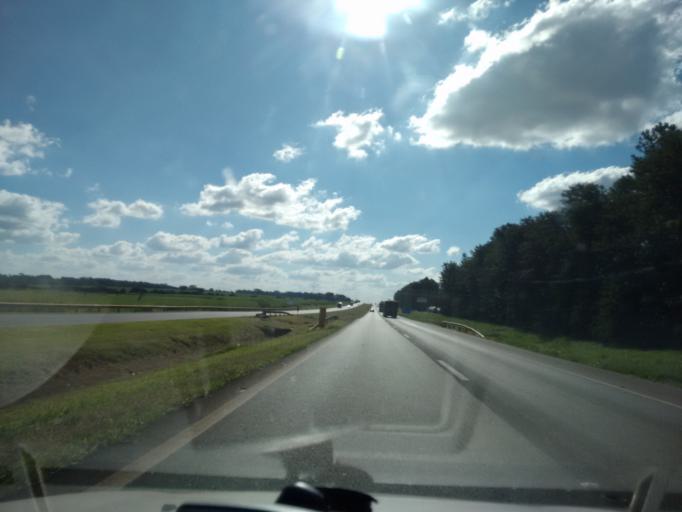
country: BR
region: Sao Paulo
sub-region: Araraquara
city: Araraquara
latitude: -21.8310
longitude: -48.1609
